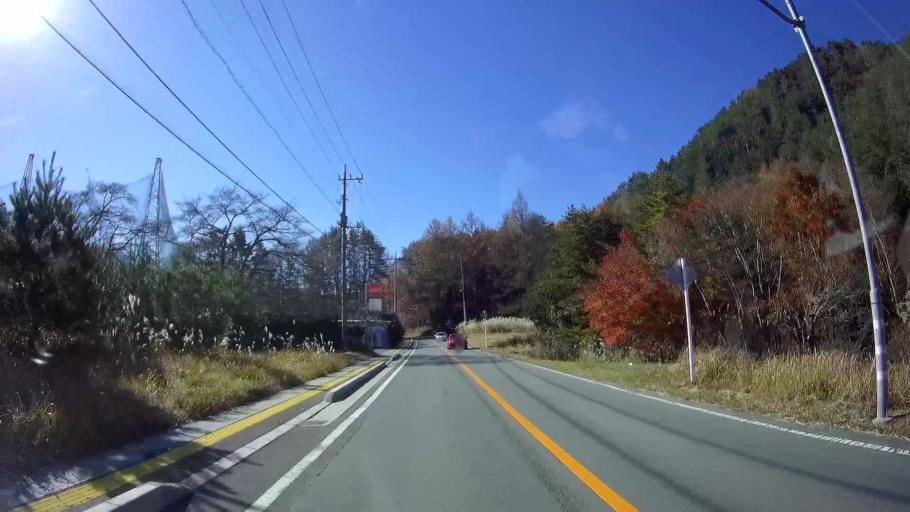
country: JP
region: Yamanashi
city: Fujikawaguchiko
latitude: 35.4937
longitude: 138.7299
